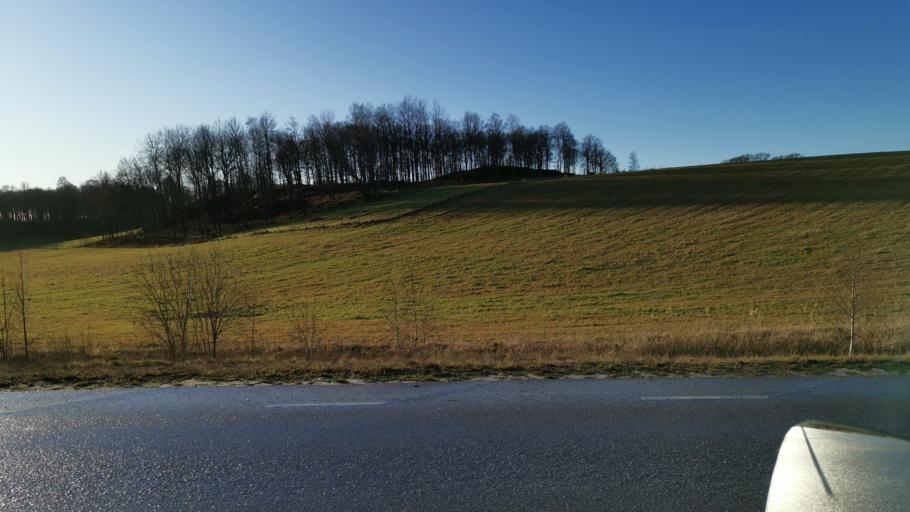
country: SE
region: Vaestra Goetaland
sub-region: Munkedals Kommun
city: Munkedal
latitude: 58.4736
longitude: 11.6598
